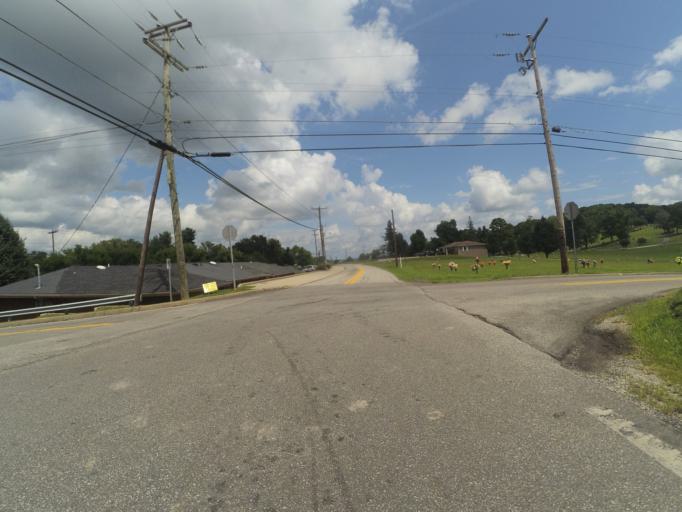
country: US
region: West Virginia
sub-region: Cabell County
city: Pea Ridge
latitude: 38.4097
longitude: -82.3336
